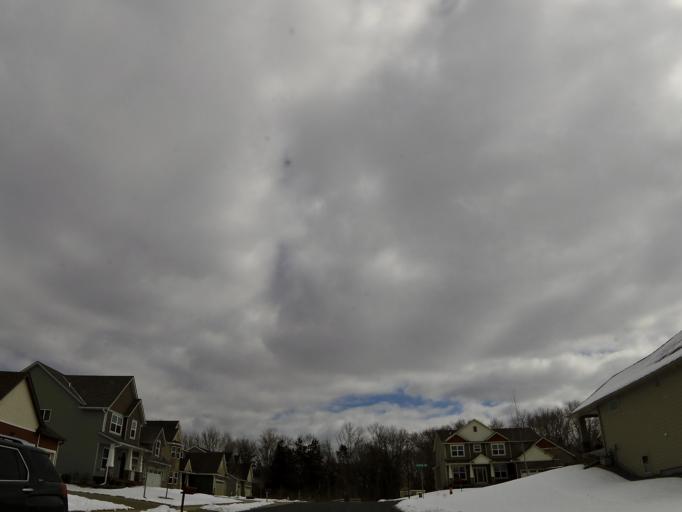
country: US
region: Minnesota
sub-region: Scott County
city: Prior Lake
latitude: 44.7677
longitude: -93.4292
